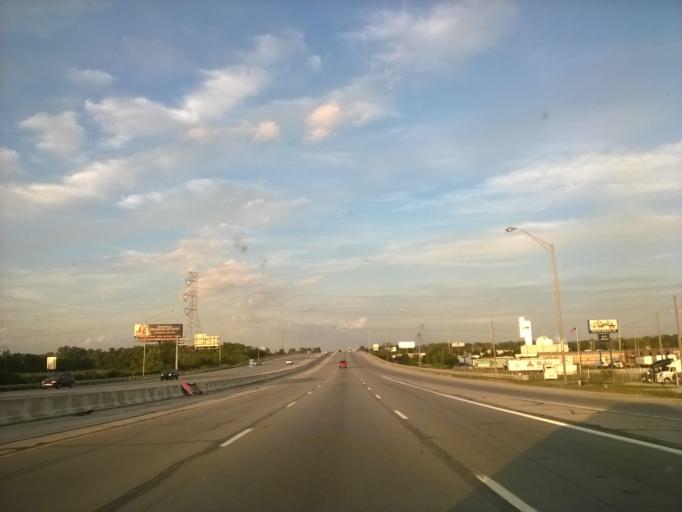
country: US
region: Indiana
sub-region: Marion County
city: Southport
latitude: 39.6966
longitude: -86.1837
